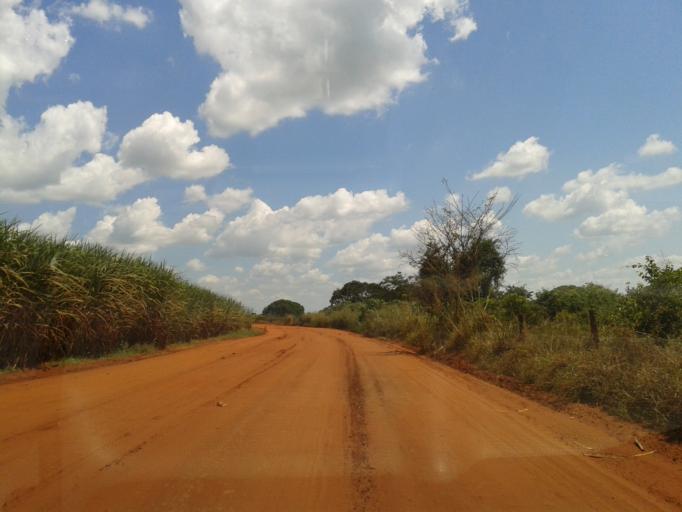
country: BR
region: Minas Gerais
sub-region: Ituiutaba
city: Ituiutaba
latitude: -19.0433
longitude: -49.7095
